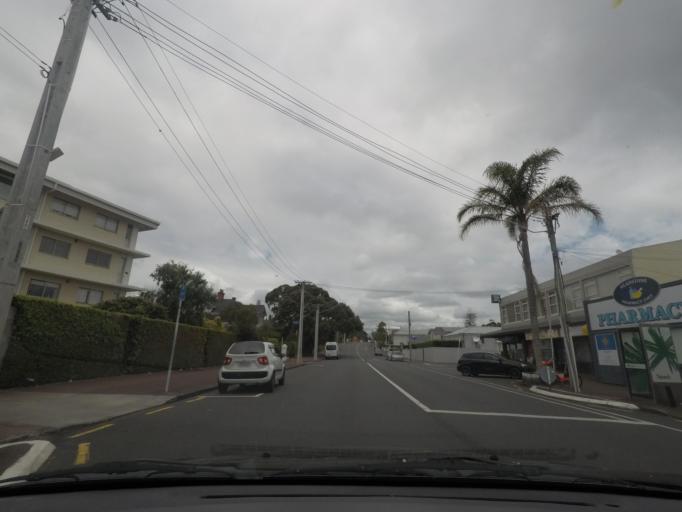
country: NZ
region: Auckland
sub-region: Auckland
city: Auckland
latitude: -36.8524
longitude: 174.7863
